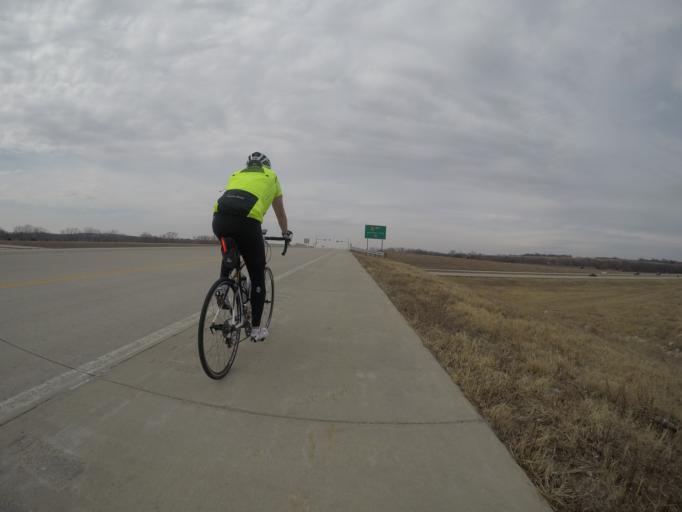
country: US
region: Kansas
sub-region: Riley County
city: Ogden
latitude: 39.1138
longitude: -96.6949
